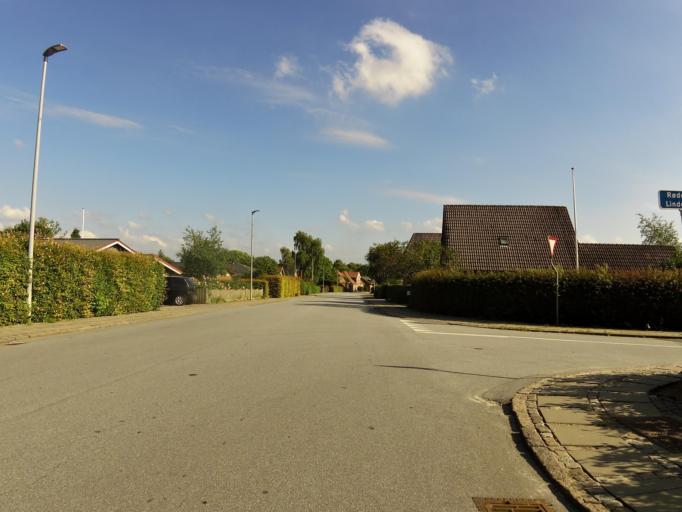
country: DK
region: South Denmark
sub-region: Vejen Kommune
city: Rodding
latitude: 55.3721
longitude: 9.0590
